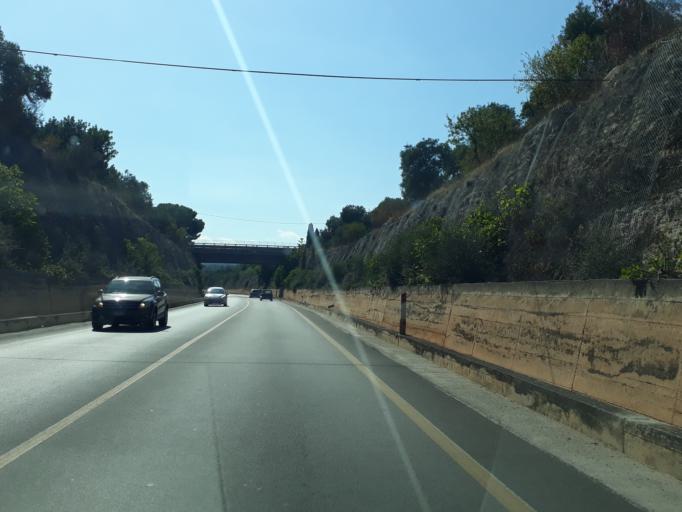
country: IT
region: Apulia
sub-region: Provincia di Brindisi
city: Fasano
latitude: 40.8383
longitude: 17.3512
